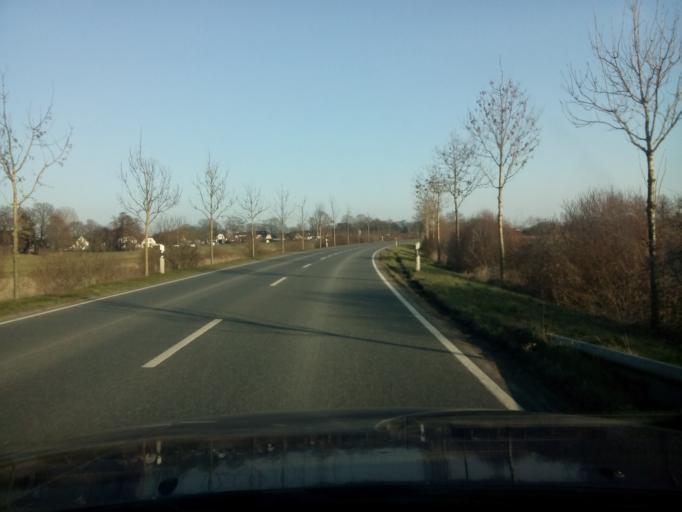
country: DE
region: Lower Saxony
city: Lilienthal
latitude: 53.1648
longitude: 8.9223
